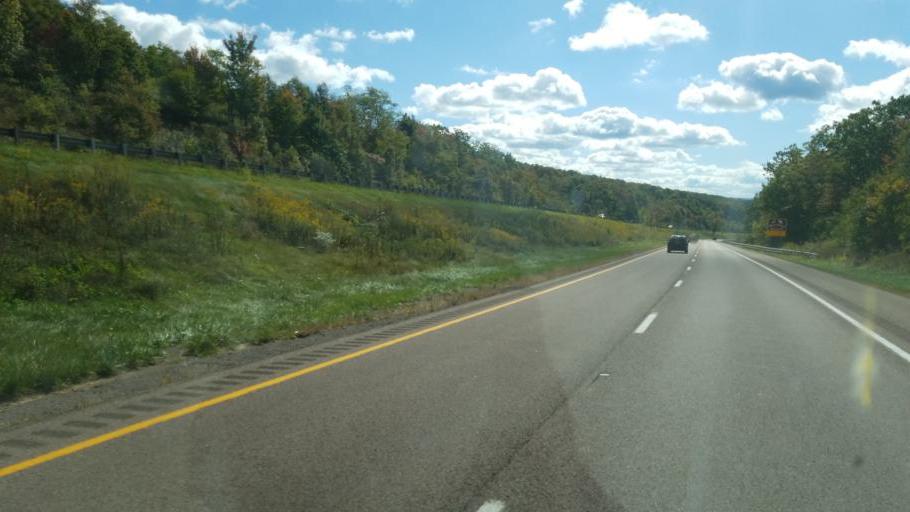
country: US
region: Maryland
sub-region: Garrett County
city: Oakland
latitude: 39.6929
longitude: -79.3429
